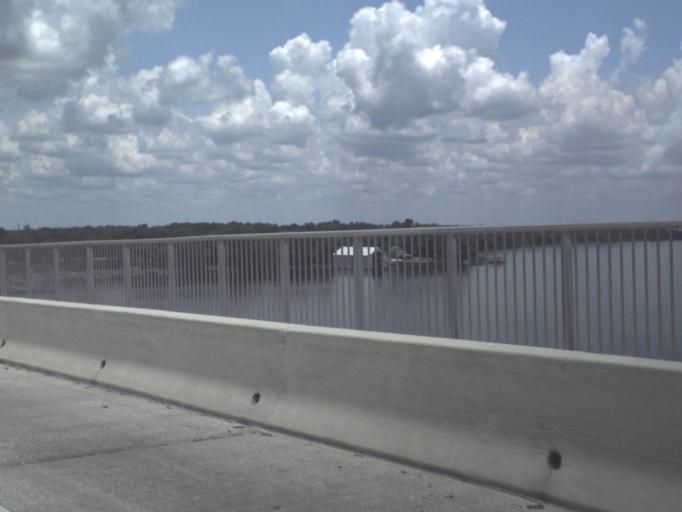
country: US
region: Florida
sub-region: Putnam County
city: Palatka
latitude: 29.6460
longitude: -81.6231
